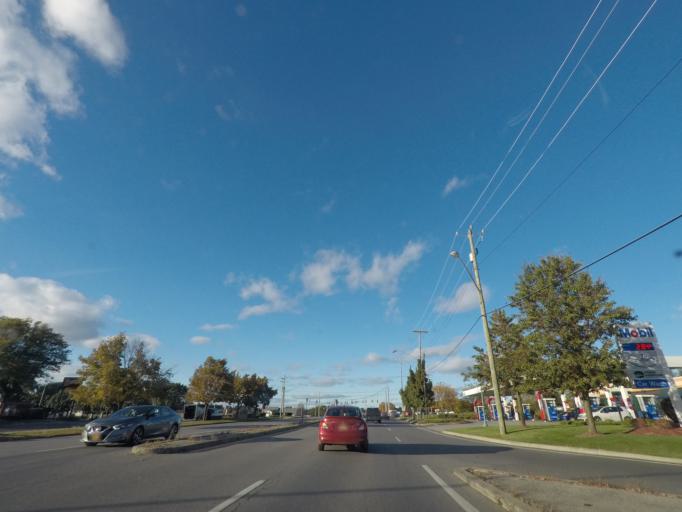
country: US
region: New York
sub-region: Saratoga County
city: Country Knolls
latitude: 42.8615
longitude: -73.7808
